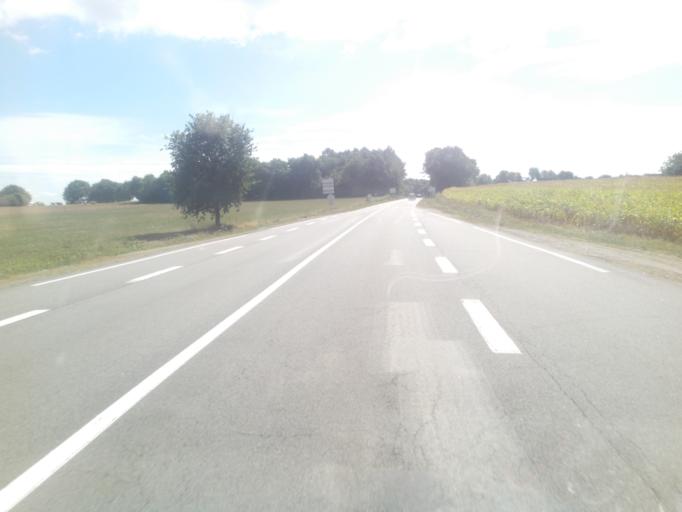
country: FR
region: Brittany
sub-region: Departement du Morbihan
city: Peaule
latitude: 47.5771
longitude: -2.3795
